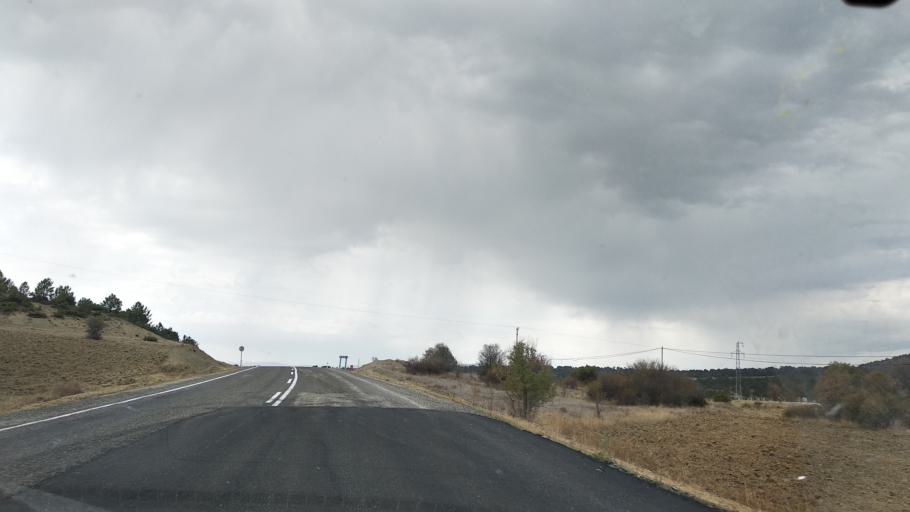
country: TR
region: Bolu
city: Seben
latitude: 40.3510
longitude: 31.4778
